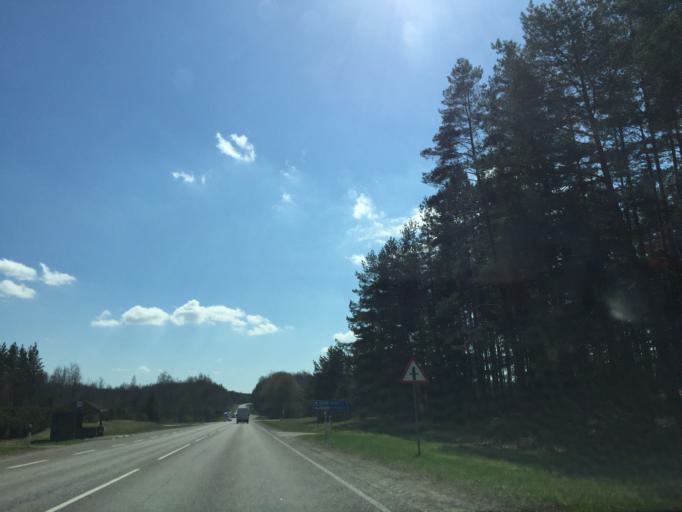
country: EE
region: Tartu
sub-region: Elva linn
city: Elva
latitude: 58.0748
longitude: 26.2057
